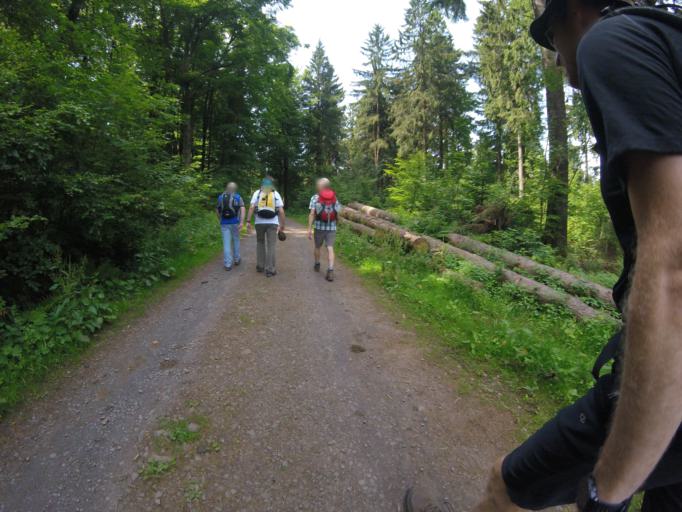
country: DE
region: Hesse
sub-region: Regierungsbezirk Giessen
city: Ulrichstein
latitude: 50.5178
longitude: 9.2369
